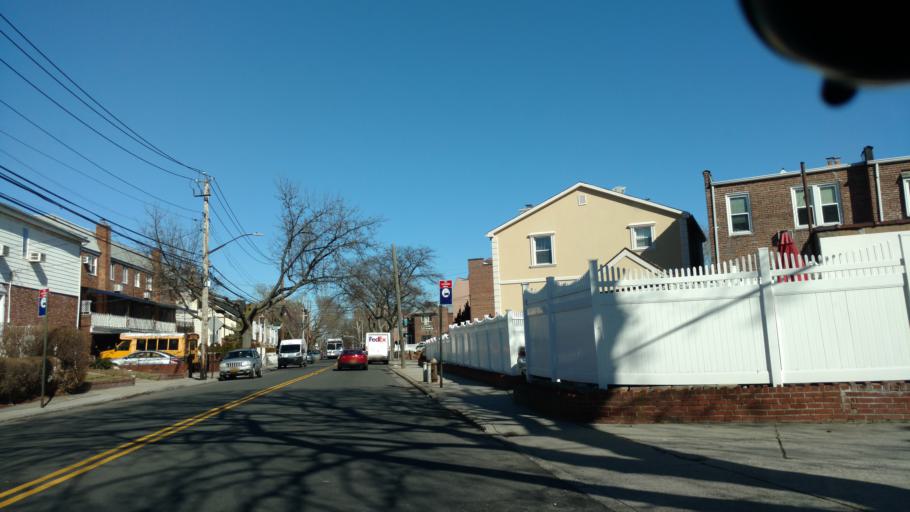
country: US
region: New York
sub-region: Queens County
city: Borough of Queens
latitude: 40.7232
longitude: -73.8742
